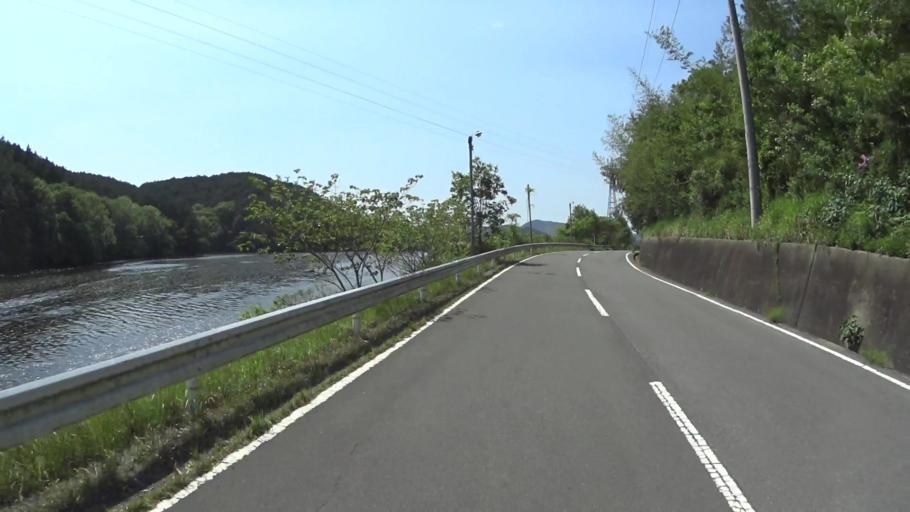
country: JP
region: Kyoto
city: Kameoka
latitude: 35.0692
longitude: 135.5635
